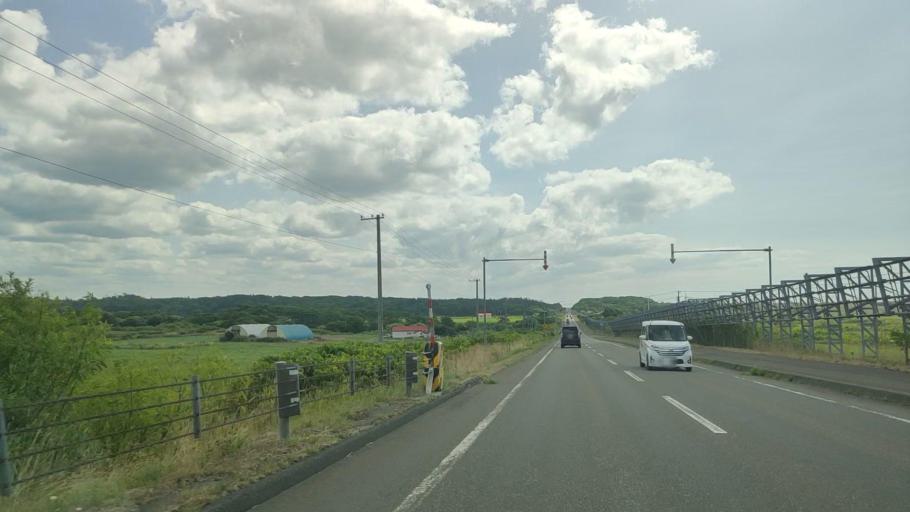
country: JP
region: Hokkaido
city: Makubetsu
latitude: 44.7769
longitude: 141.7915
